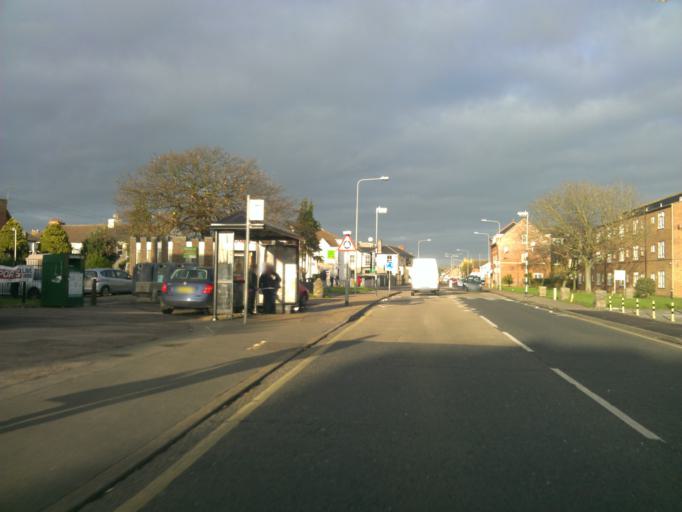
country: GB
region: England
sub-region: Essex
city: Clacton-on-Sea
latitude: 51.7961
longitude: 1.1491
